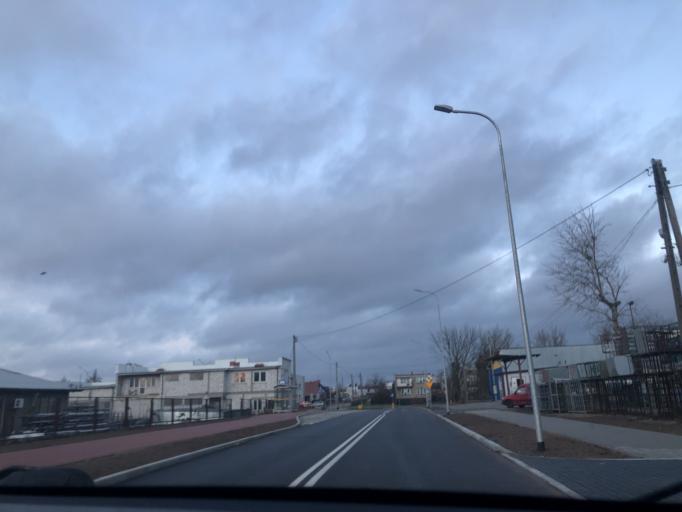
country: PL
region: Podlasie
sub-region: Lomza
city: Lomza
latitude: 53.1737
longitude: 22.0637
